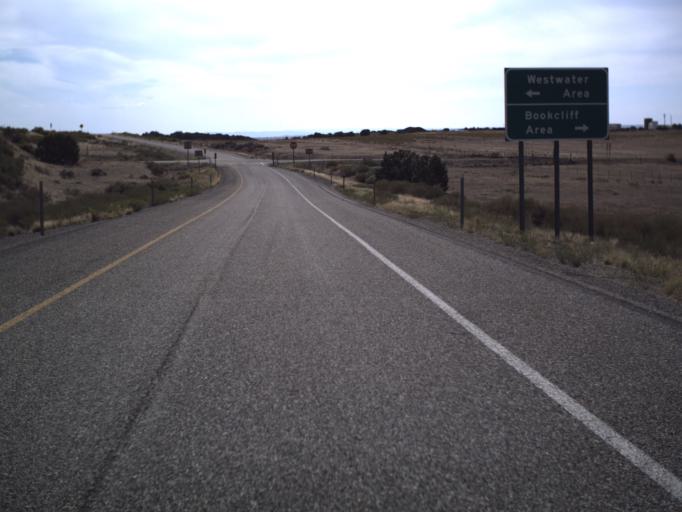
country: US
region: Colorado
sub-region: Mesa County
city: Loma
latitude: 39.1763
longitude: -109.1265
